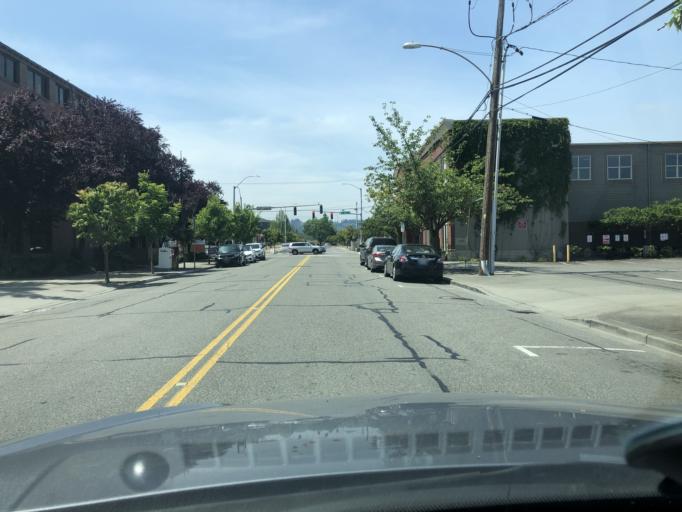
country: US
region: Washington
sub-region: King County
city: Kent
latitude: 47.3809
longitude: -122.2364
